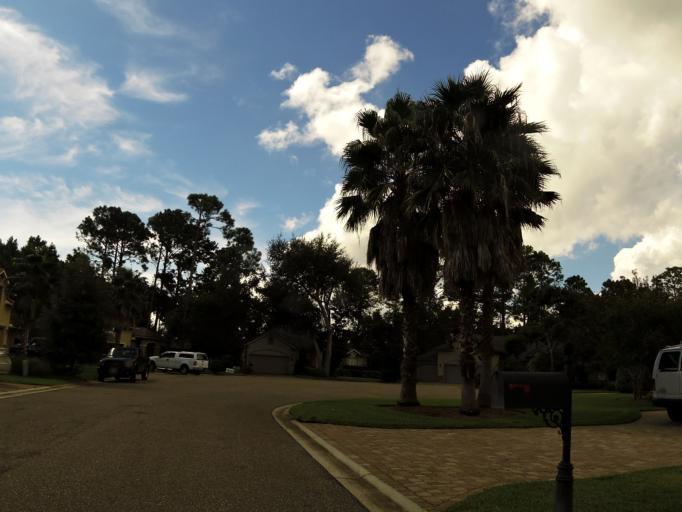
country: US
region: Florida
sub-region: Nassau County
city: Fernandina Beach
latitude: 30.6253
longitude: -81.4600
